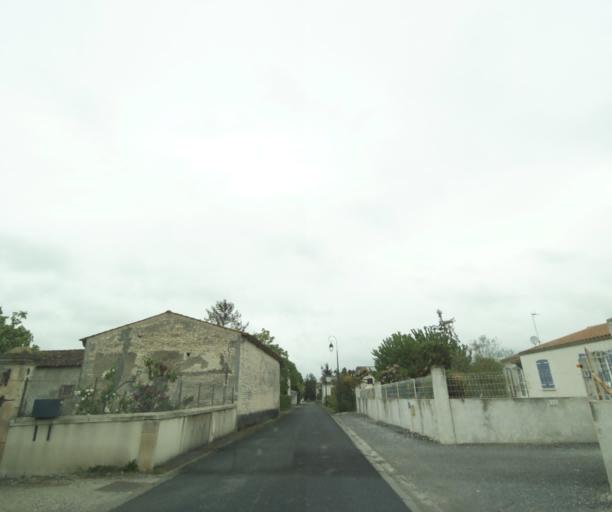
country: FR
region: Poitou-Charentes
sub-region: Departement de la Charente-Maritime
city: Perignac
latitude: 45.6496
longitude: -0.5037
